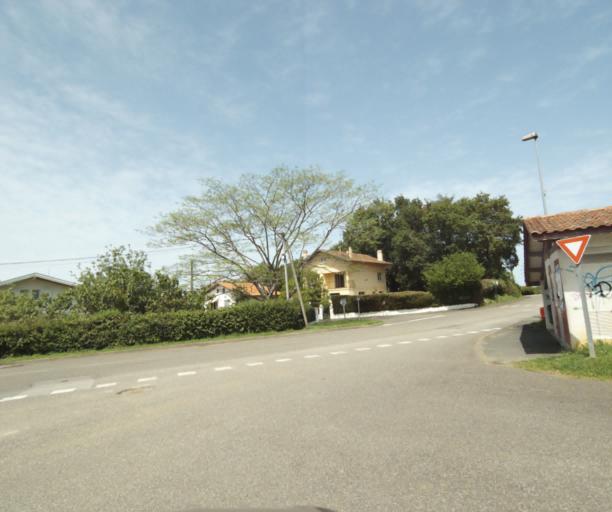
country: FR
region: Aquitaine
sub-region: Departement des Pyrenees-Atlantiques
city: Mouguerre
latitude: 43.4665
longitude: -1.4410
